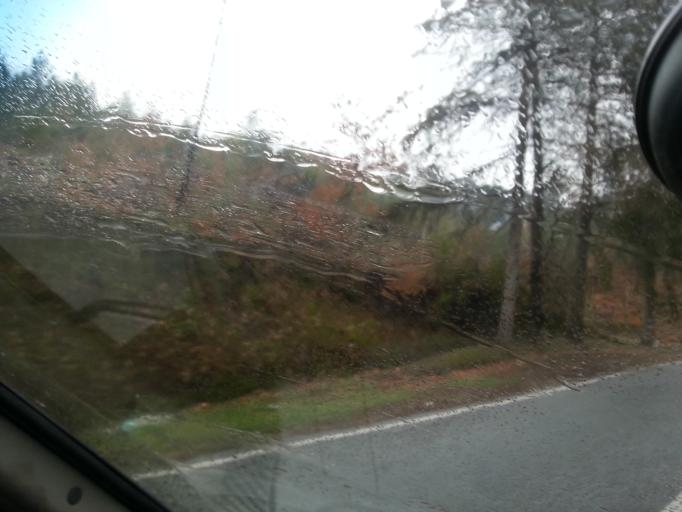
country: PT
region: Viseu
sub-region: Mangualde
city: Mangualde
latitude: 40.6325
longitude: -7.8038
